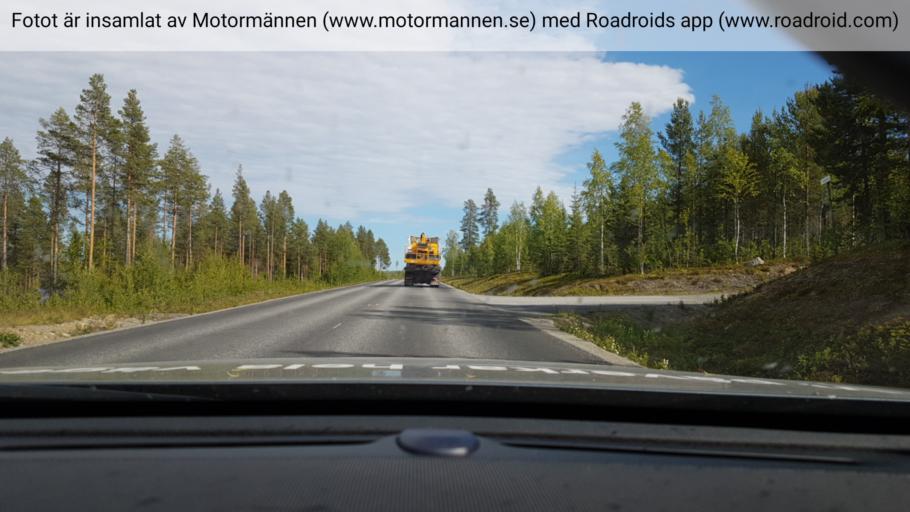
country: SE
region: Vaesterbotten
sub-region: Lycksele Kommun
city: Soderfors
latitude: 64.8395
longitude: 17.9834
